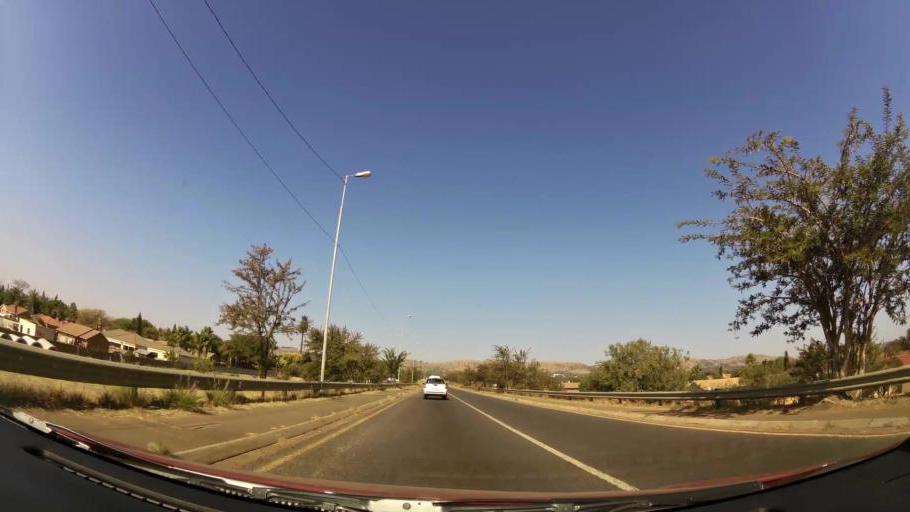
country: ZA
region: North-West
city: Ga-Rankuwa
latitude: -25.6565
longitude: 28.1019
